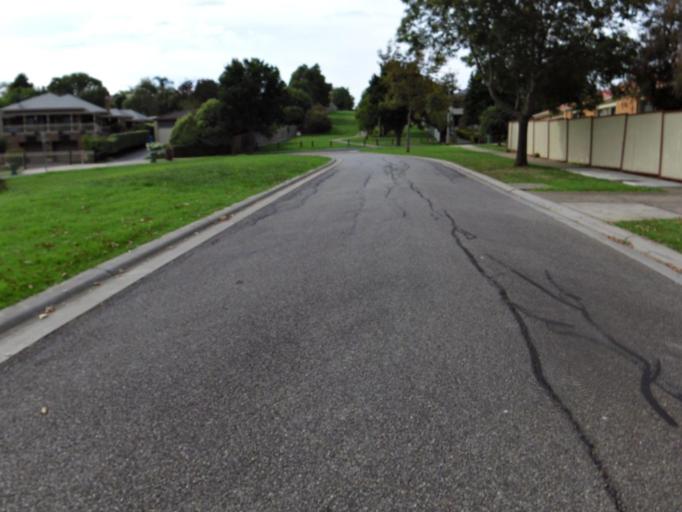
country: AU
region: Victoria
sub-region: Casey
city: Berwick
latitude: -38.0415
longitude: 145.3507
